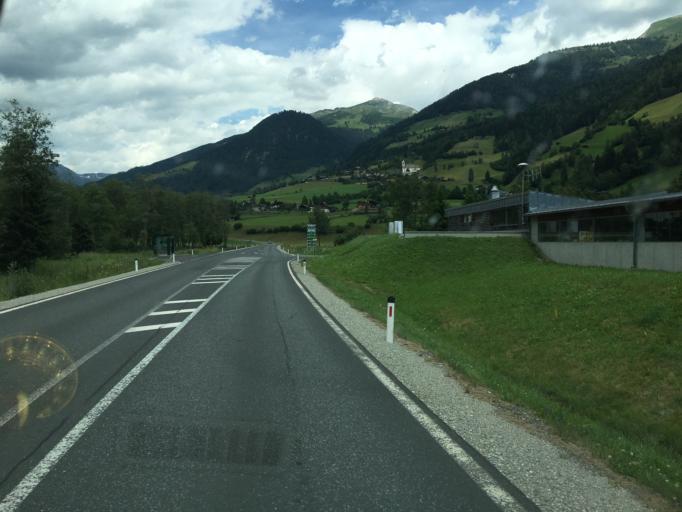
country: AT
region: Carinthia
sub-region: Politischer Bezirk Spittal an der Drau
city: Grosskirchheim
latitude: 46.9488
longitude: 12.8987
